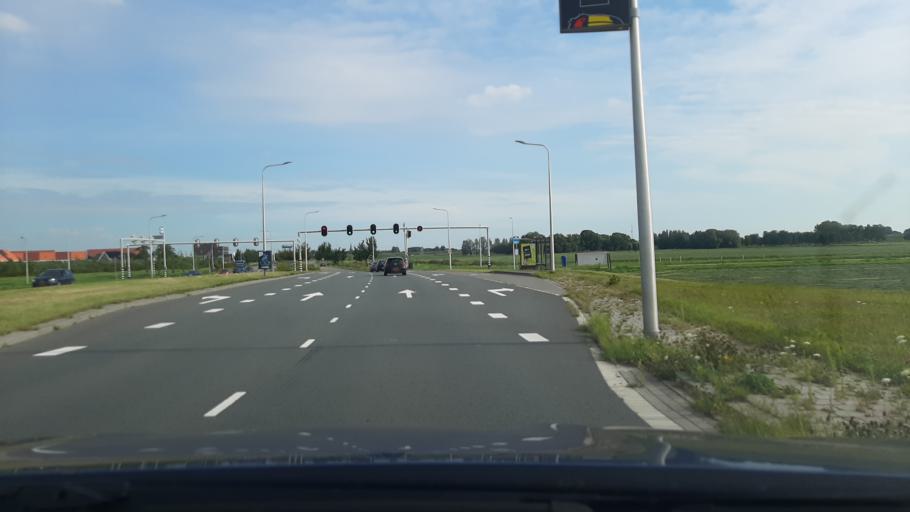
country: NL
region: Friesland
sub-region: Gemeente Leeuwarden
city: Goutum
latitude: 53.1674
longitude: 5.7916
